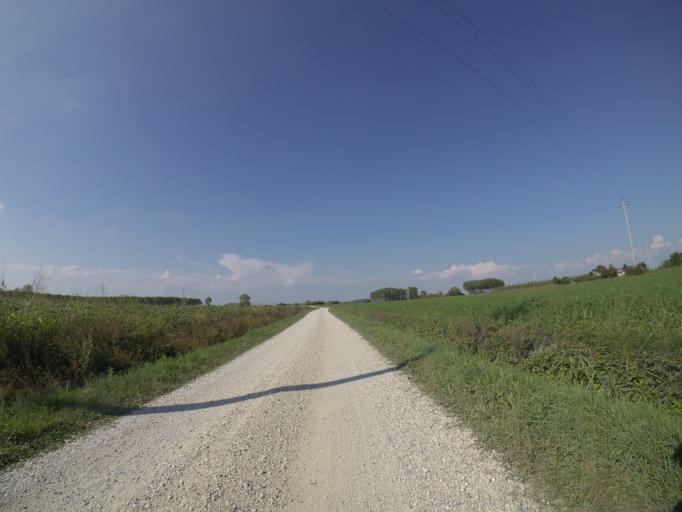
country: IT
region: Friuli Venezia Giulia
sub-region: Provincia di Udine
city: Muzzana del Turgnano
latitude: 45.8194
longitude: 13.1177
